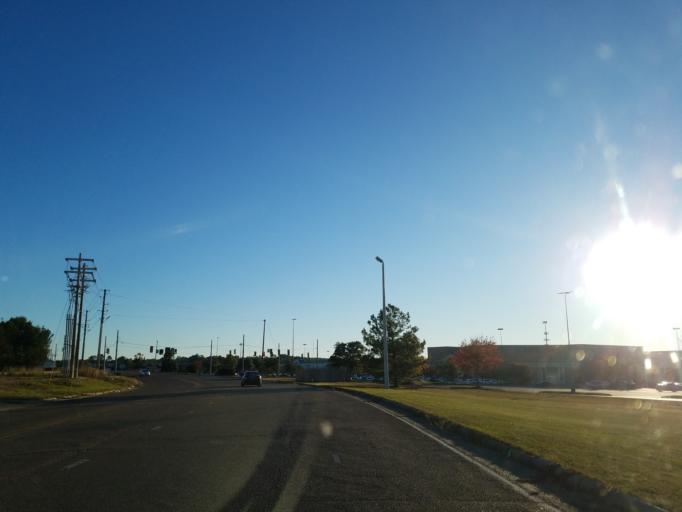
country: US
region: Mississippi
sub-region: Lamar County
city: Arnold Line
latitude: 31.3284
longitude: -89.3733
